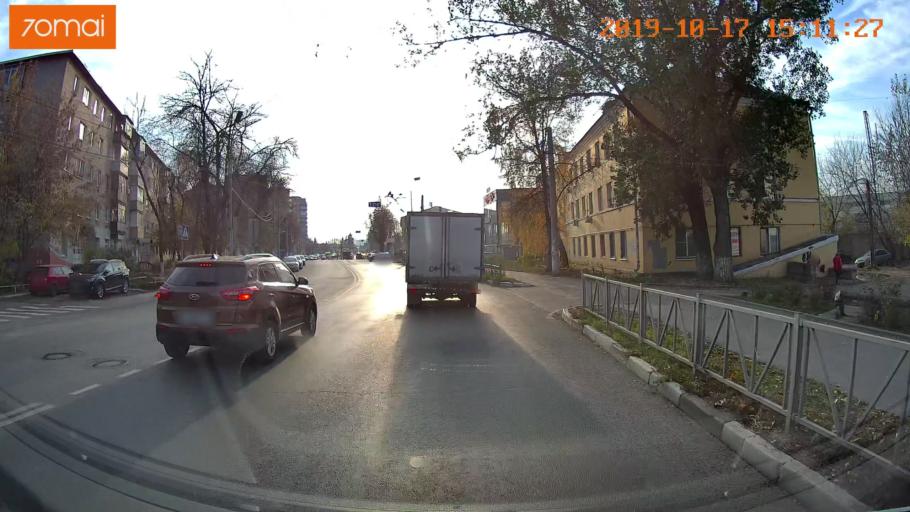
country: RU
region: Rjazan
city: Ryazan'
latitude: 54.6321
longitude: 39.7065
